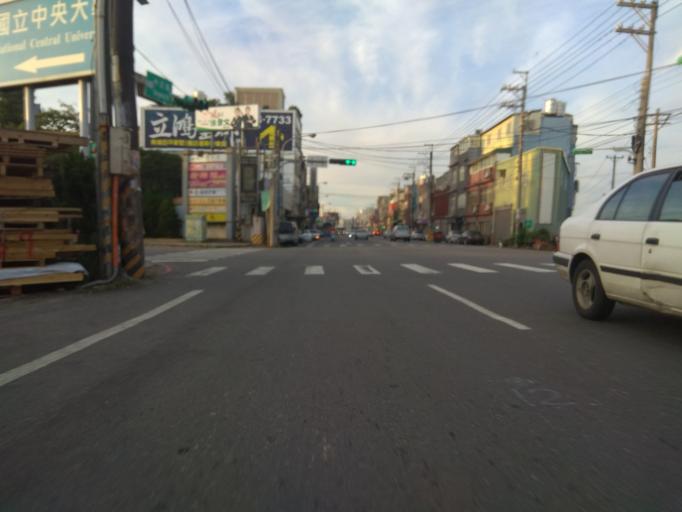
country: TW
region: Taiwan
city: Taoyuan City
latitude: 24.9680
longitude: 121.2027
